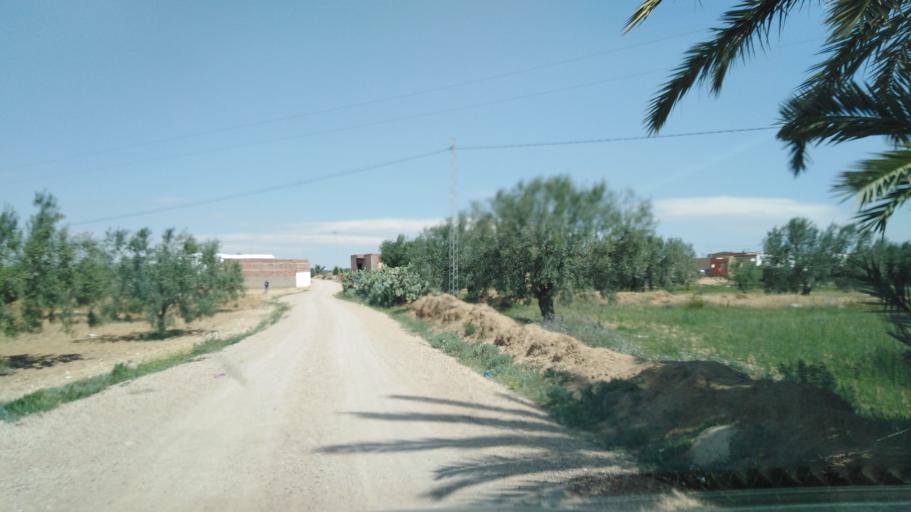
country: TN
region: Safaqis
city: Sfax
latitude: 34.7615
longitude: 10.5245
